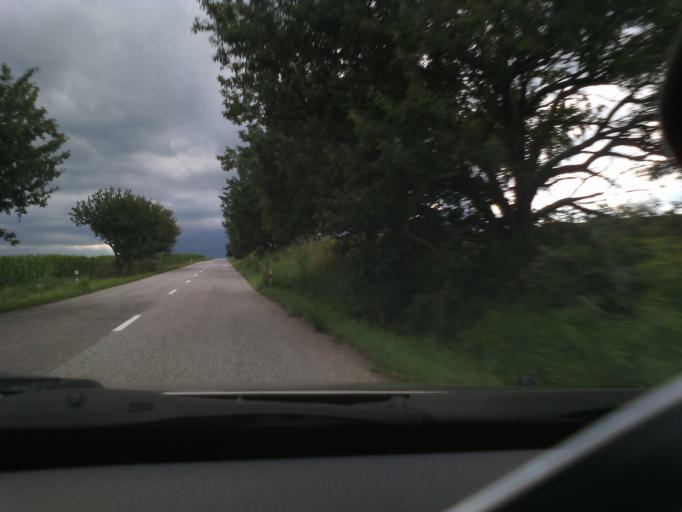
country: SK
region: Presovsky
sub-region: Okres Presov
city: Kezmarok
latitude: 49.1068
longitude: 20.3865
